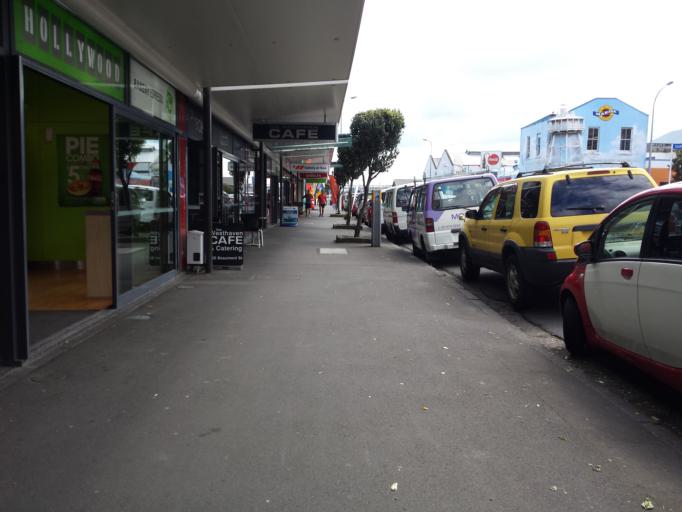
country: NZ
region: Auckland
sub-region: Auckland
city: Auckland
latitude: -36.8443
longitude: 174.7532
